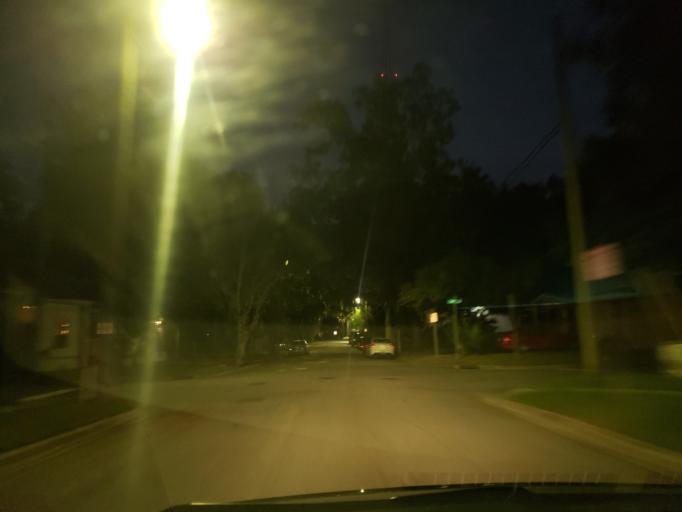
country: US
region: Georgia
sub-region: Chatham County
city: Thunderbolt
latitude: 32.0475
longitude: -81.0797
